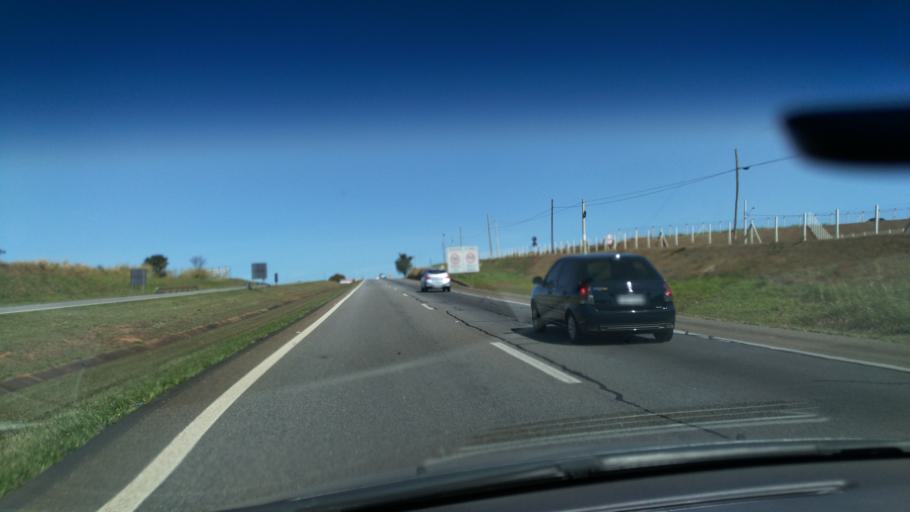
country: BR
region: Sao Paulo
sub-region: Santo Antonio De Posse
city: Santo Antonio de Posse
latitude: -22.5429
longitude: -46.9977
